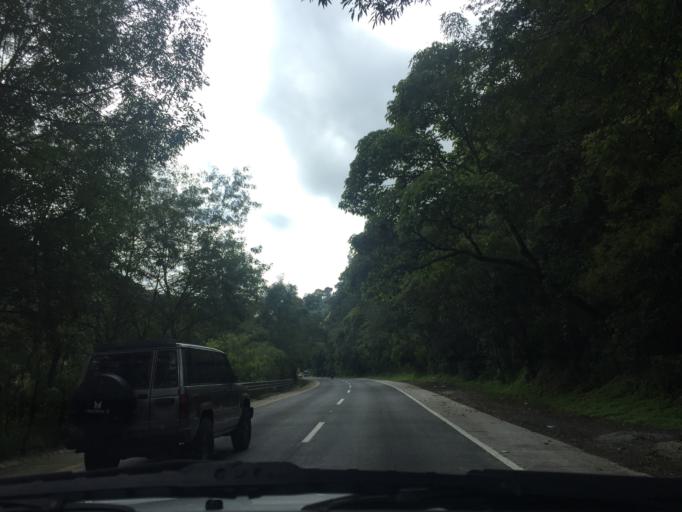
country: GT
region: Sacatepequez
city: Santa Lucia Milpas Altas
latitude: 14.5626
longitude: -90.6940
